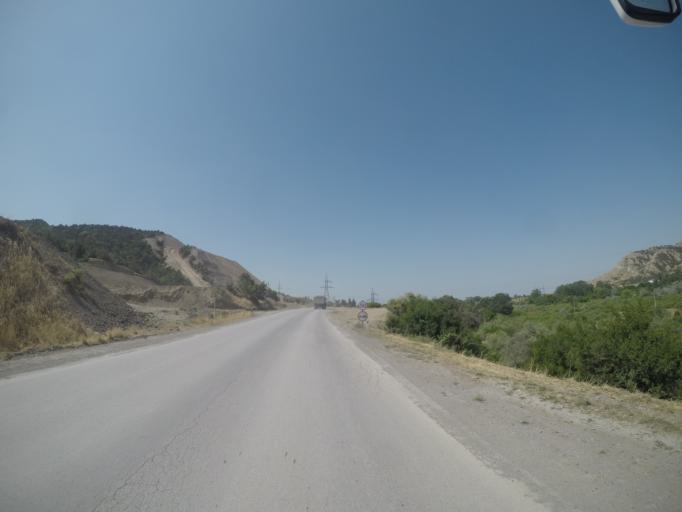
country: AZ
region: Agdas
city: Agdas
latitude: 40.7127
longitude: 47.5548
